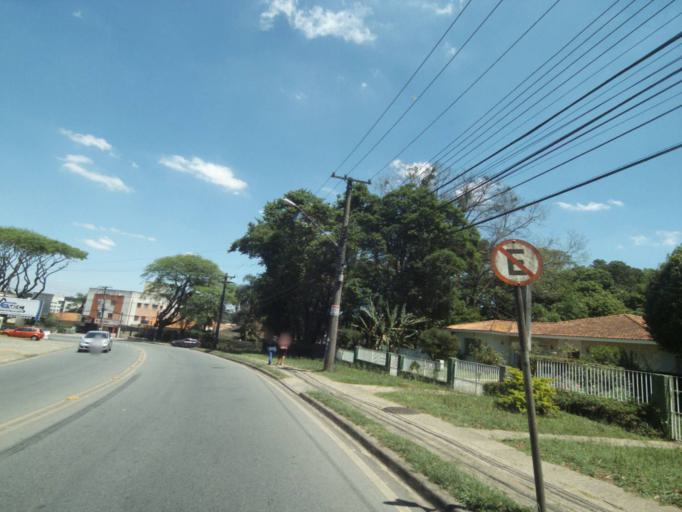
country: BR
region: Parana
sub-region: Curitiba
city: Curitiba
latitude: -25.3880
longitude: -49.2227
